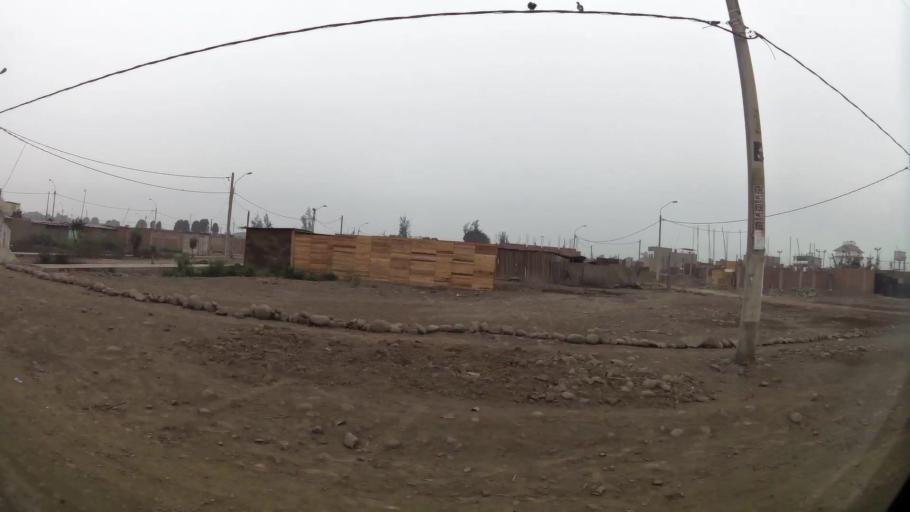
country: PE
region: Lima
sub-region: Lima
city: Carabayllo
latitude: -11.8600
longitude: -77.0172
